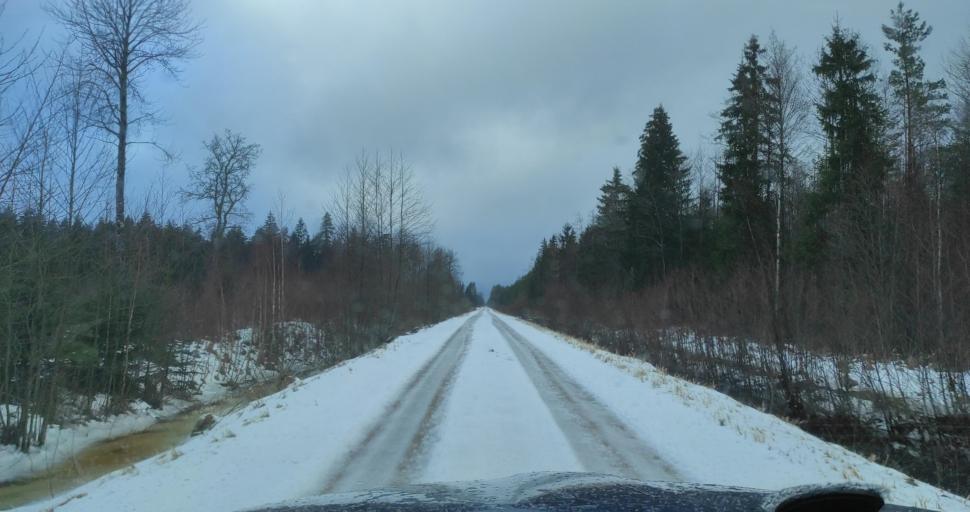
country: LV
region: Dundaga
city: Dundaga
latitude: 57.3982
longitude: 22.1132
